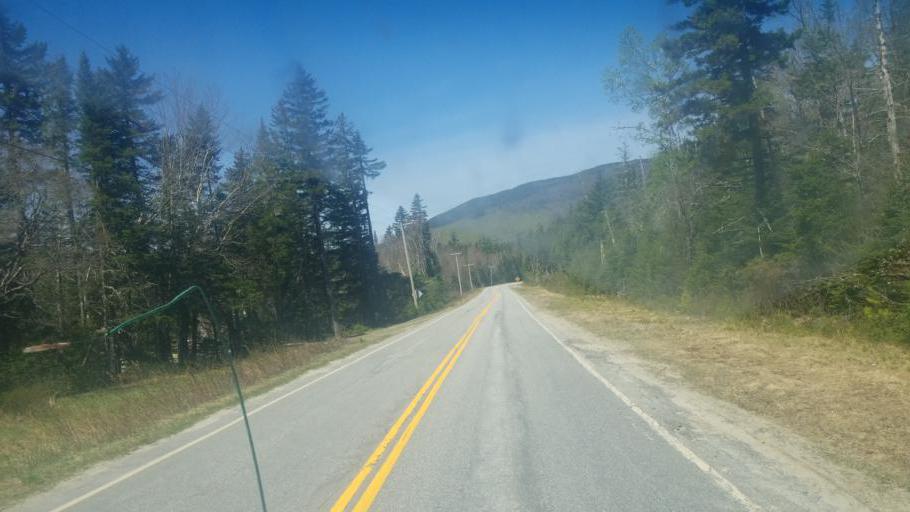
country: US
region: New Hampshire
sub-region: Coos County
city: Jefferson
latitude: 44.2606
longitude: -71.4040
